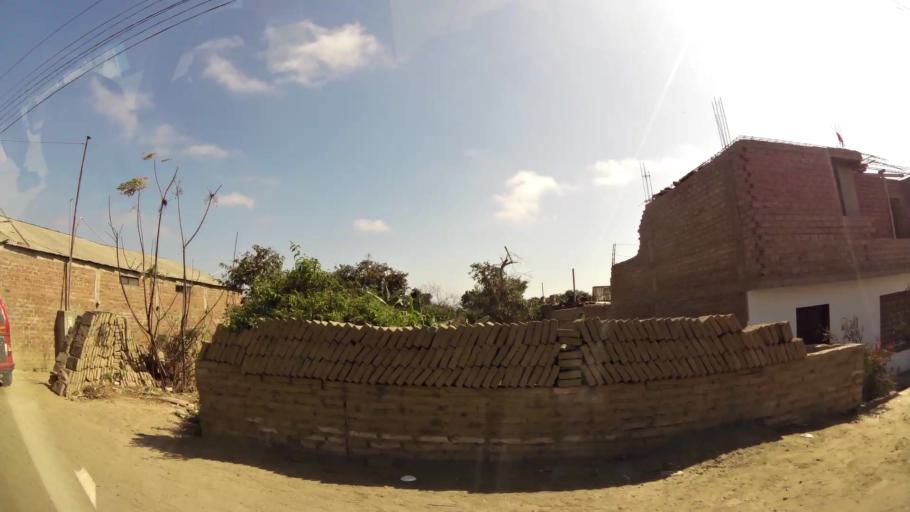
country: PE
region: Ica
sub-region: Provincia de Chincha
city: Sunampe
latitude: -13.4233
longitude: -76.1581
